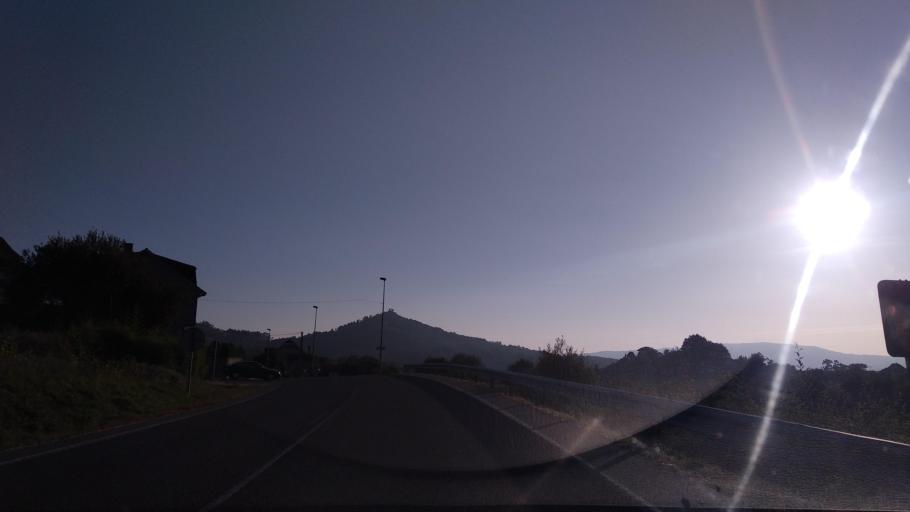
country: ES
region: Galicia
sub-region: Provincia de Pontevedra
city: Redondela
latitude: 42.3419
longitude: -8.5618
